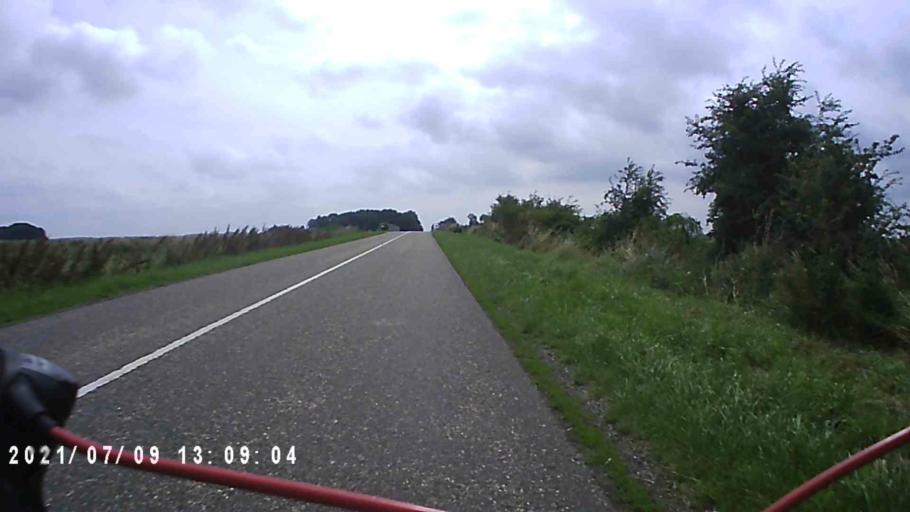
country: NL
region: Groningen
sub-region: Gemeente  Oldambt
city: Winschoten
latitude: 53.1299
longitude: 7.1152
